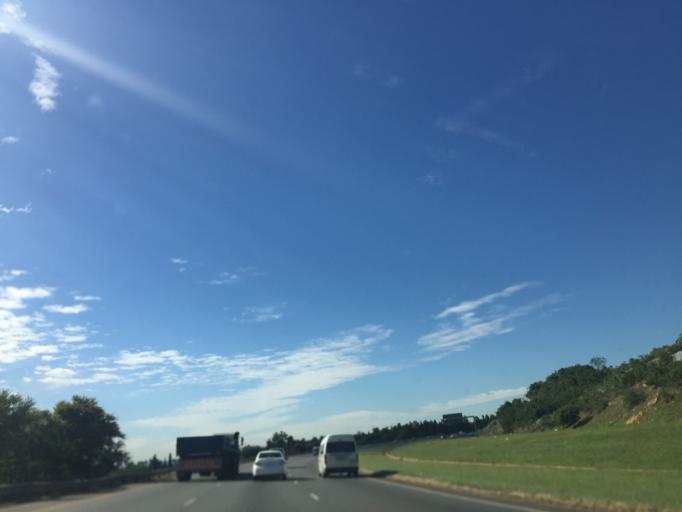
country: ZA
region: Gauteng
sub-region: Ekurhuleni Metropolitan Municipality
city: Germiston
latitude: -26.2740
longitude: 28.1040
